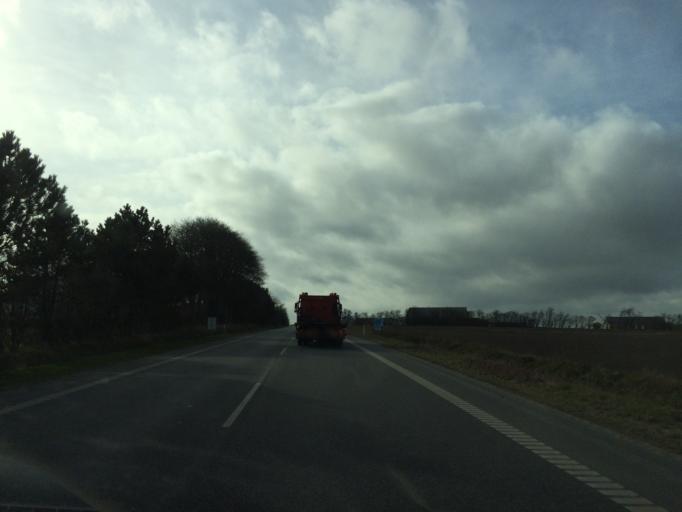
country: DK
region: Central Jutland
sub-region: Randers Kommune
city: Langa
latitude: 56.4755
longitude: 9.9268
